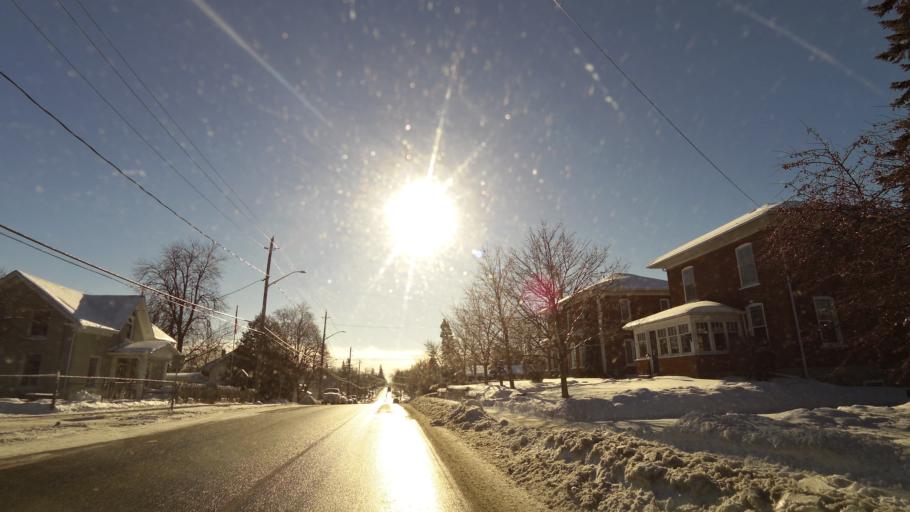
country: CA
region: Ontario
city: Quinte West
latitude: 44.3069
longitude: -77.7931
